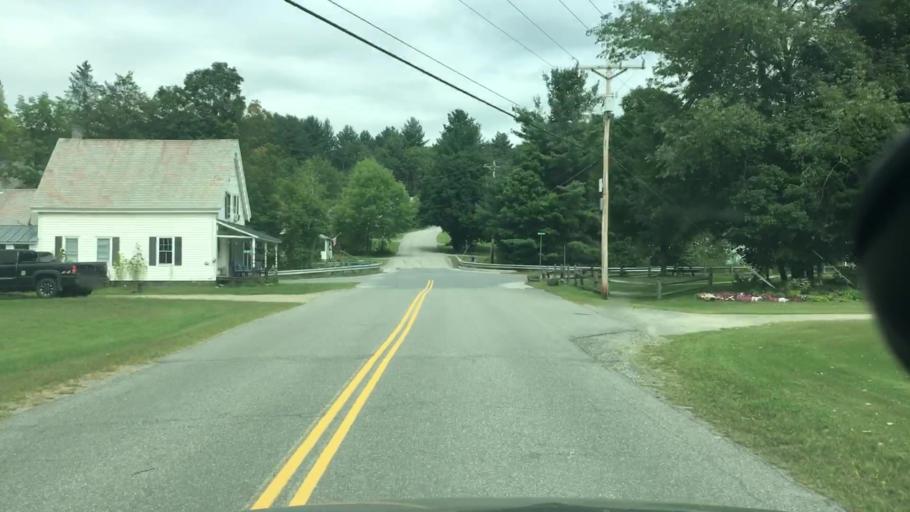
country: US
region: Massachusetts
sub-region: Franklin County
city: Colrain
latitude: 42.7869
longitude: -72.7706
